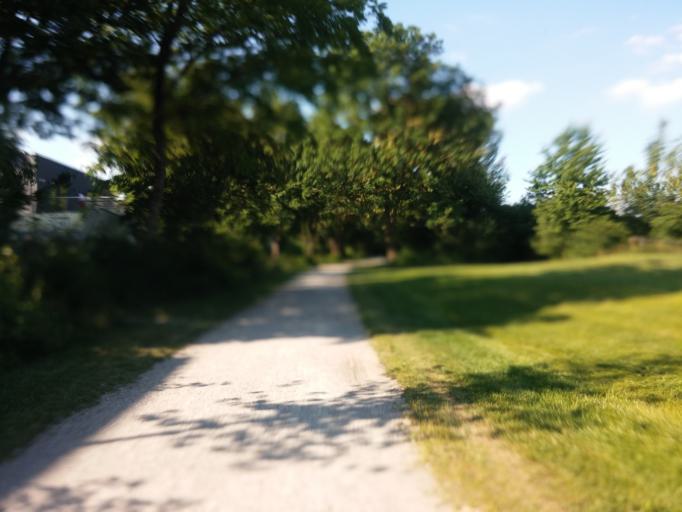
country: DE
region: Bavaria
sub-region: Upper Bavaria
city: Neubiberg
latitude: 48.1333
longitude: 11.6707
